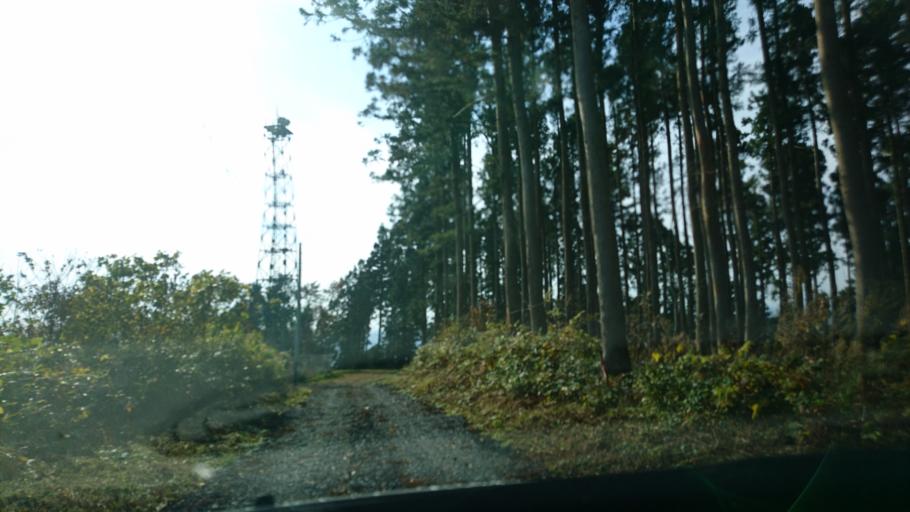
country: JP
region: Iwate
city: Ichinoseki
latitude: 38.9816
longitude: 141.1631
